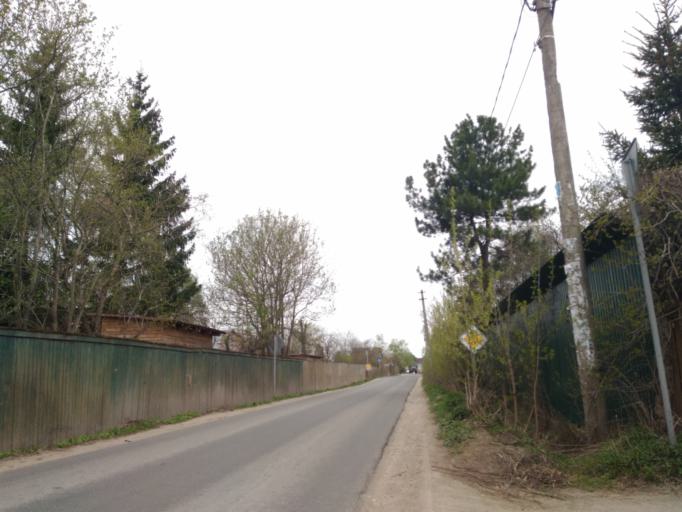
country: RU
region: Moskovskaya
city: Dedovsk
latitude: 55.8513
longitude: 37.1438
